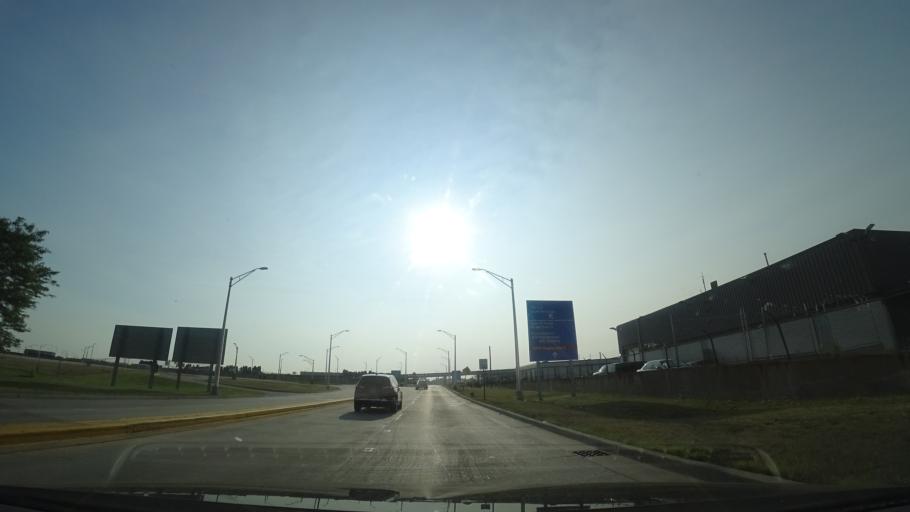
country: US
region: Illinois
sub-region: Cook County
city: Rosemont
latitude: 41.9765
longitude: -87.8855
